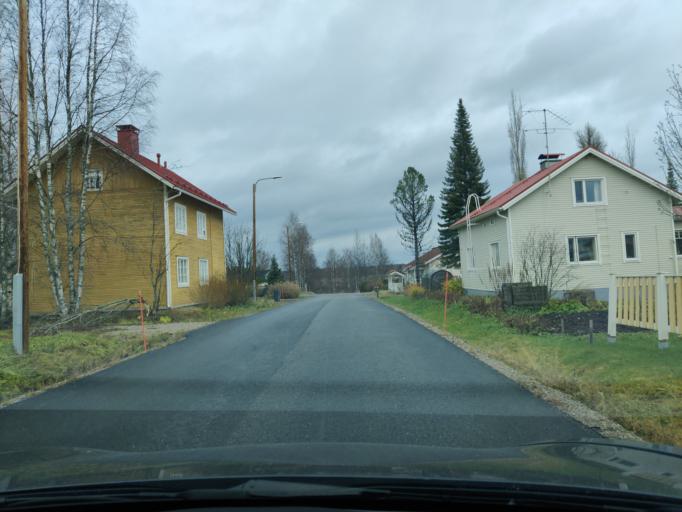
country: FI
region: Northern Savo
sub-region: Ylae-Savo
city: Kiuruvesi
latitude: 63.6499
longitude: 26.6345
